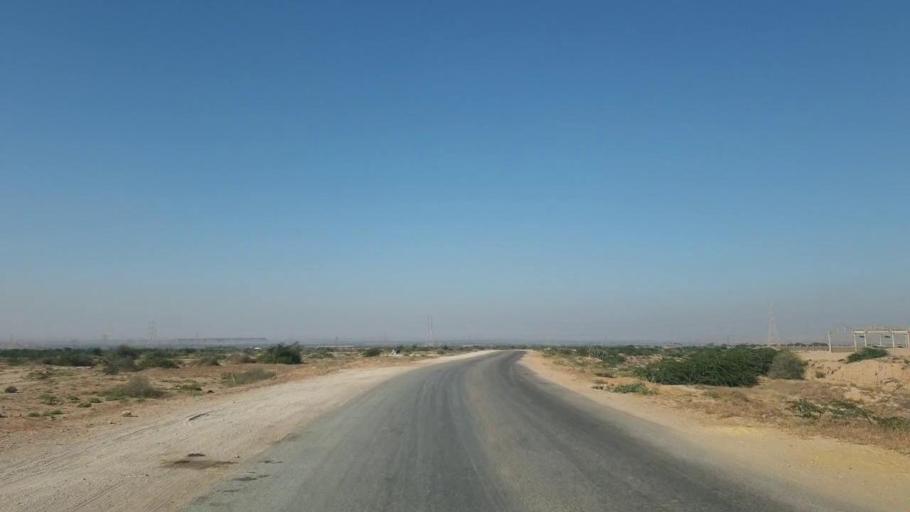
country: PK
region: Sindh
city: Gharo
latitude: 25.1569
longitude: 67.6640
